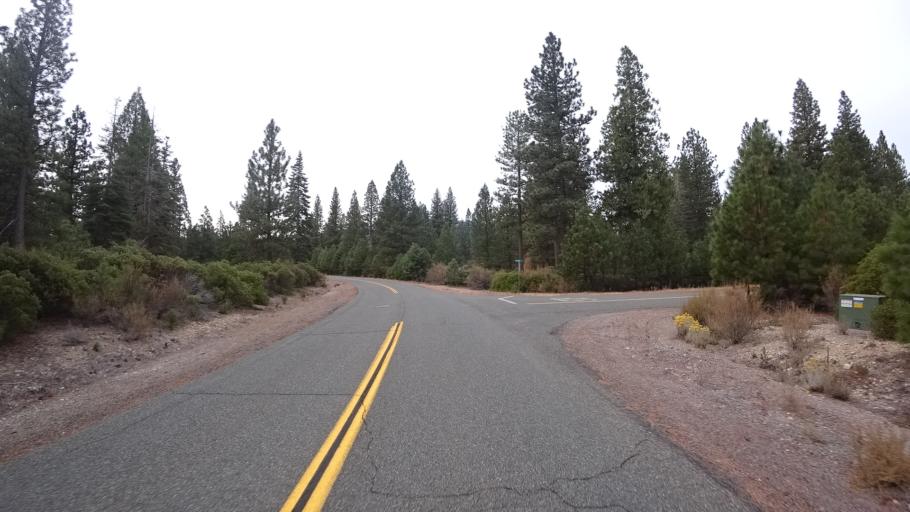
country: US
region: California
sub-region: Siskiyou County
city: Weed
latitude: 41.4129
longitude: -122.3708
